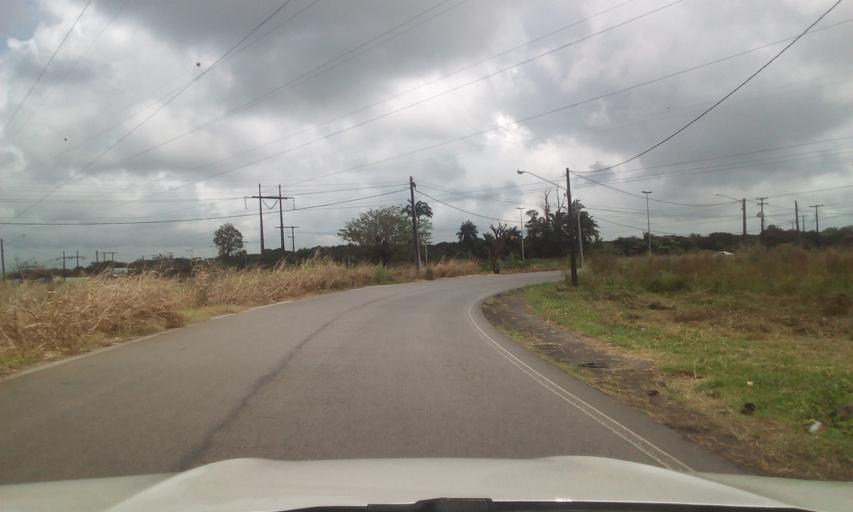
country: BR
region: Pernambuco
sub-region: Recife
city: Recife
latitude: -8.0691
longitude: -34.9446
